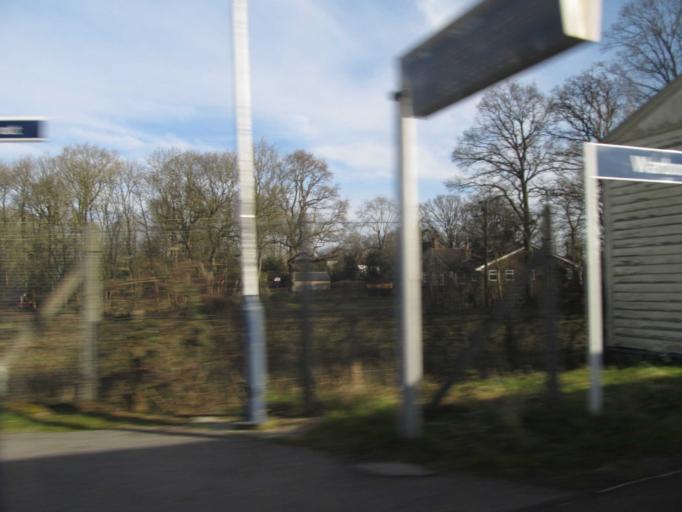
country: GB
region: England
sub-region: Surrey
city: Normandy
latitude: 51.2445
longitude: -0.6684
